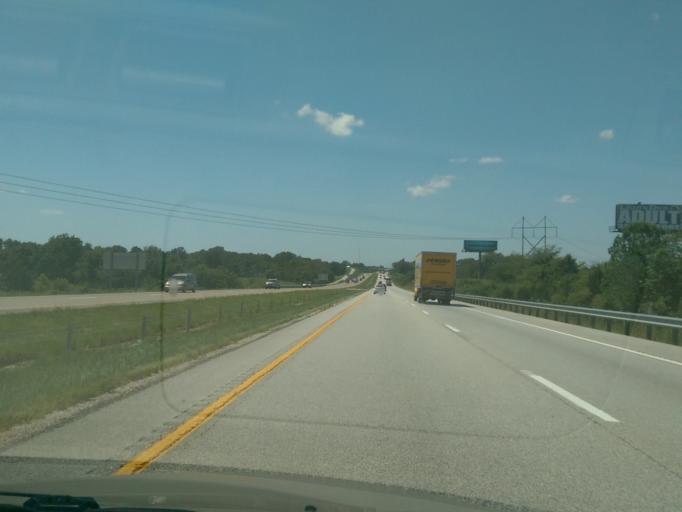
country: US
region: Missouri
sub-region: Cooper County
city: Boonville
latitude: 38.9356
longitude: -92.7859
